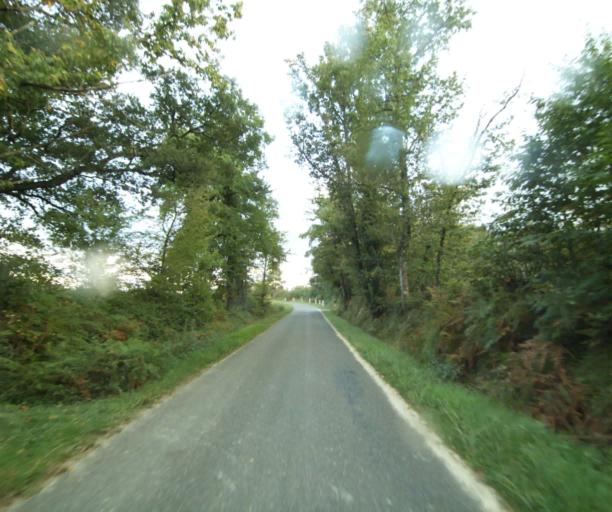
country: FR
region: Midi-Pyrenees
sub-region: Departement du Gers
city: Cazaubon
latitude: 43.9060
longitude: -0.0890
